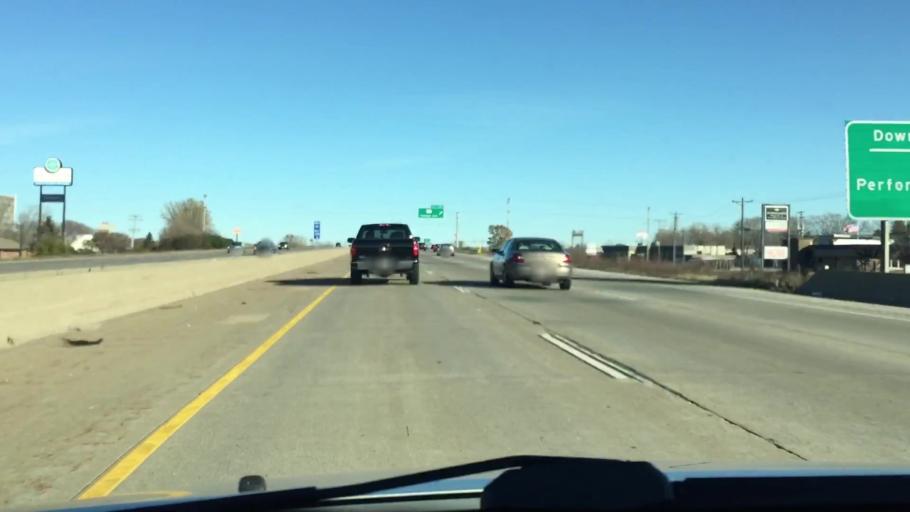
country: US
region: Wisconsin
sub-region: Outagamie County
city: Appleton
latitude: 44.2565
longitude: -88.4663
